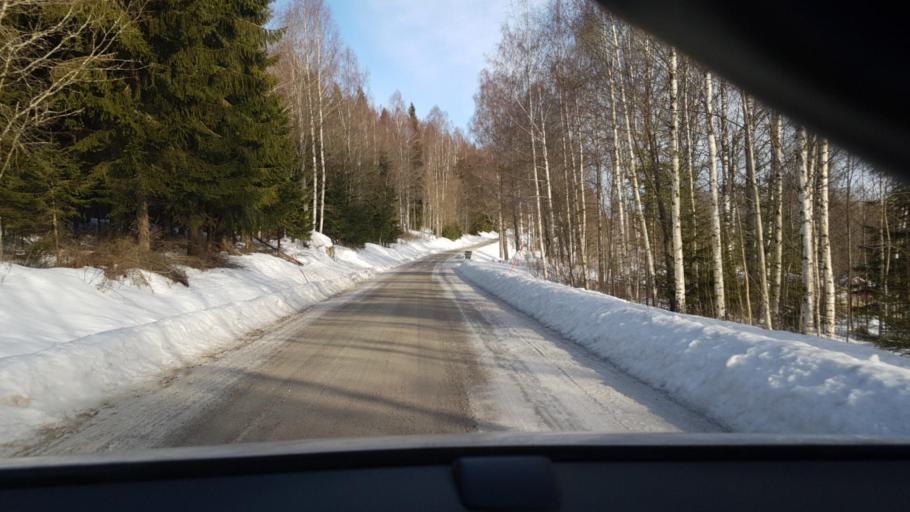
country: SE
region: Vaermland
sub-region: Eda Kommun
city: Amotfors
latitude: 59.7370
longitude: 12.2785
